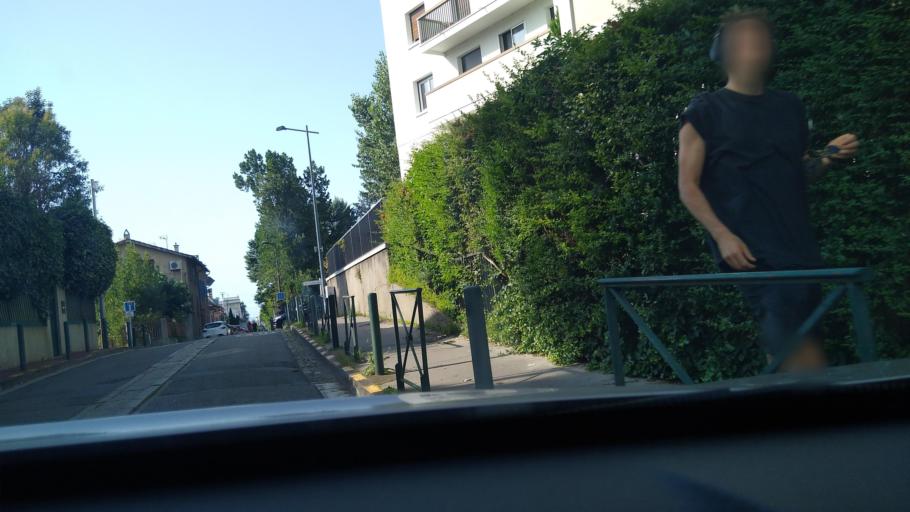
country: FR
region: Midi-Pyrenees
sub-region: Departement de la Haute-Garonne
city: Toulouse
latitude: 43.6144
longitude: 1.4609
